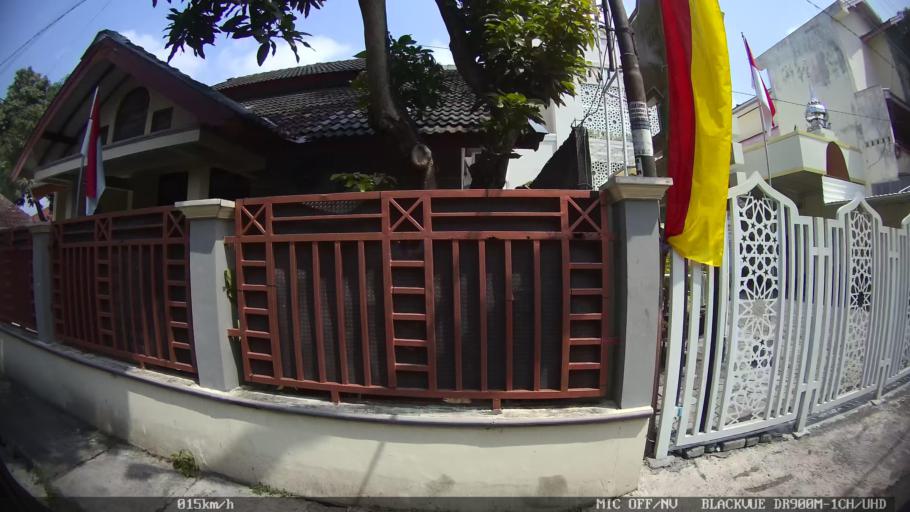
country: ID
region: Daerah Istimewa Yogyakarta
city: Yogyakarta
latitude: -7.8081
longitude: 110.3866
